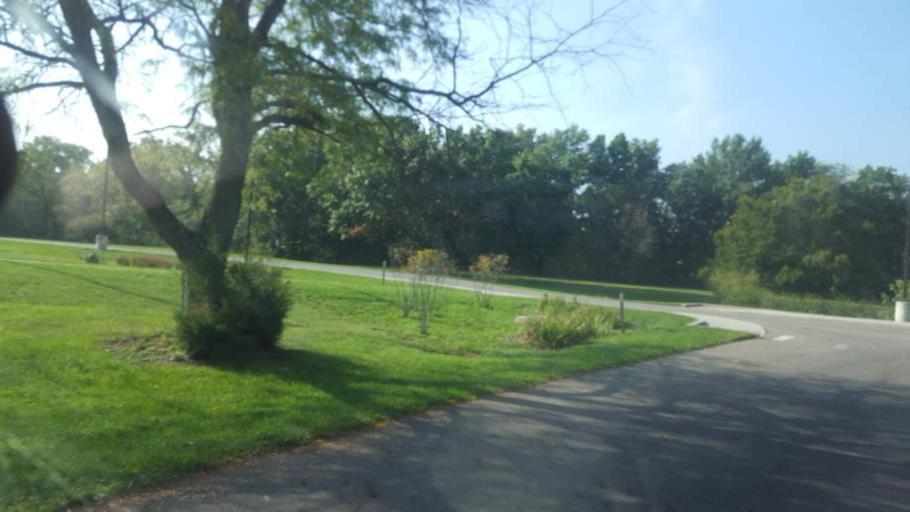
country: US
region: Ohio
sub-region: Franklin County
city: Worthington
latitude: 40.0689
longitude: -83.0149
